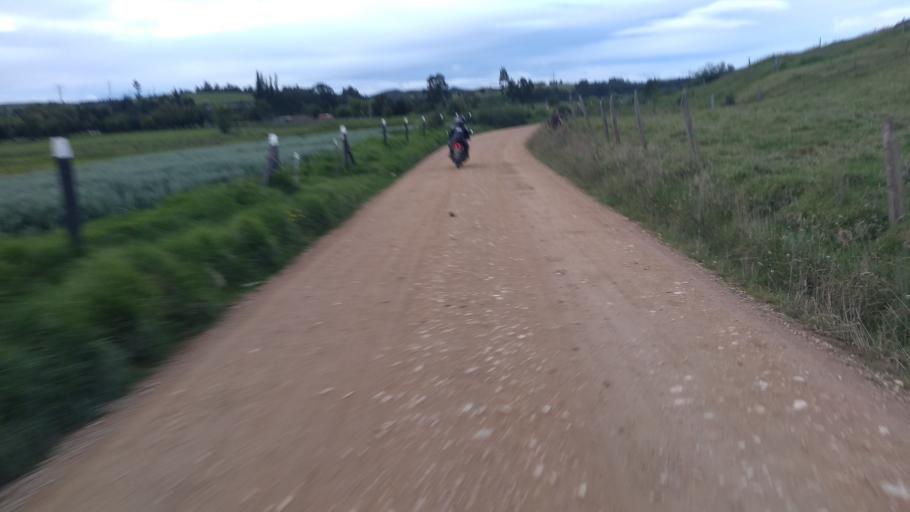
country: CO
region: Boyaca
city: Toca
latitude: 5.6184
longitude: -73.1691
